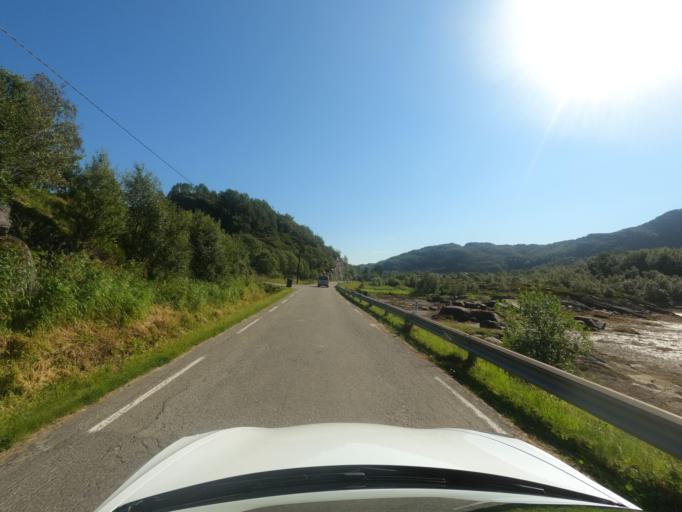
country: NO
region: Nordland
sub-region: Hadsel
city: Stokmarknes
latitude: 68.3044
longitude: 15.0085
